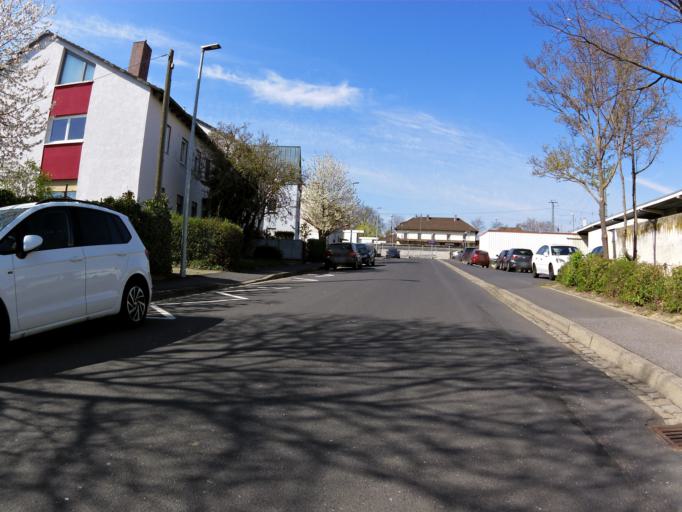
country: DE
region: Bavaria
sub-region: Regierungsbezirk Unterfranken
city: Rottendorf
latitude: 49.7922
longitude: 10.0307
